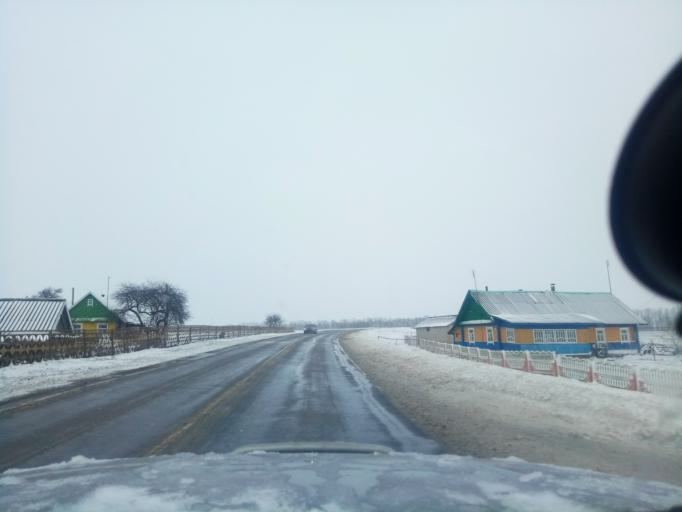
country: BY
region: Minsk
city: Haradzyeya
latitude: 53.3328
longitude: 26.5415
